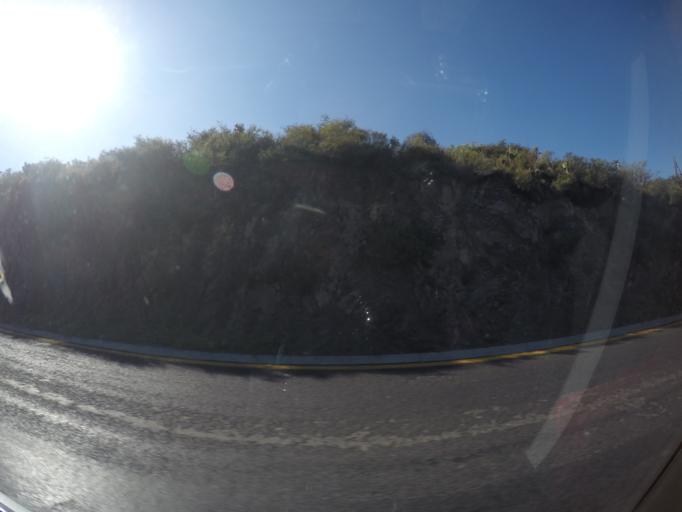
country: MX
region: Hidalgo
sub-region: Mineral de la Reforma
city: Rio de la Soledad
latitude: 20.1188
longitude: -98.7065
